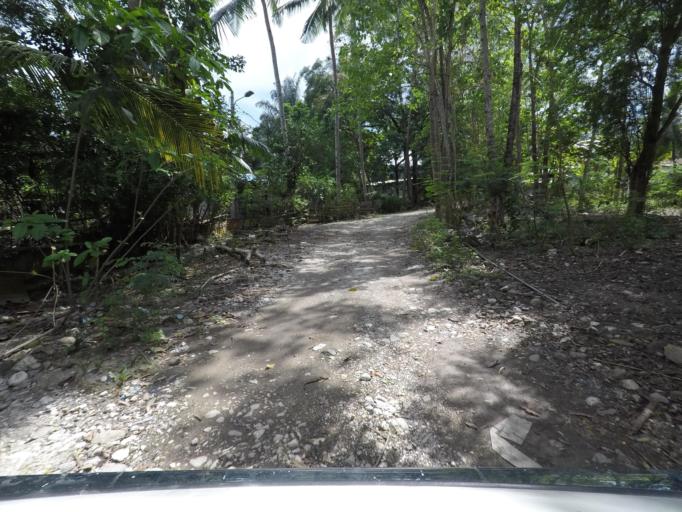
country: TL
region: Viqueque
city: Viqueque
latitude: -8.8707
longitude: 126.3679
